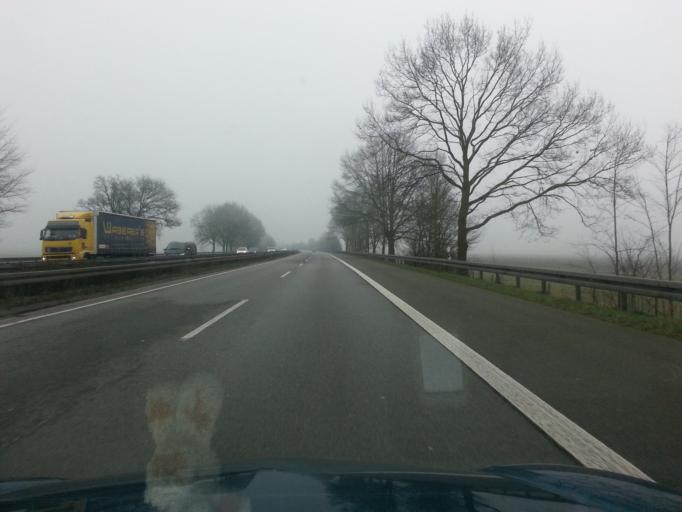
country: DE
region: North Rhine-Westphalia
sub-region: Regierungsbezirk Dusseldorf
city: Emmerich
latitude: 51.8696
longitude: 6.2063
